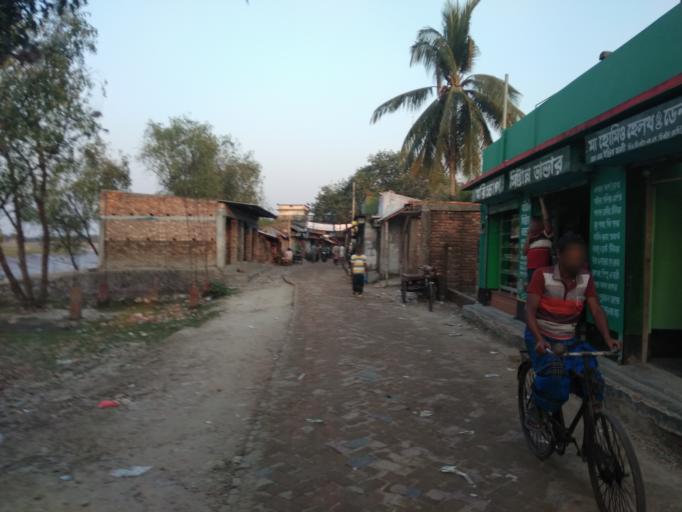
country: BD
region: Khulna
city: Satkhira
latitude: 22.5481
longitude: 89.1745
